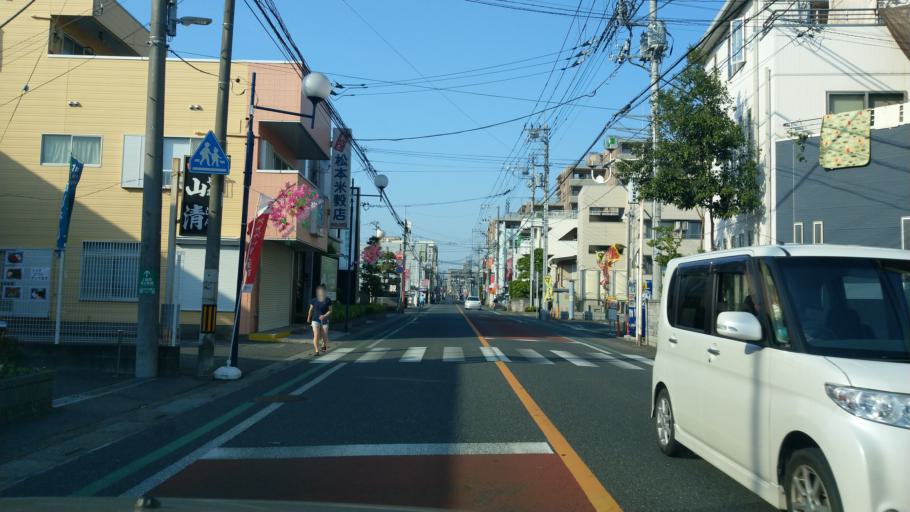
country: JP
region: Saitama
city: Kamifukuoka
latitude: 35.8673
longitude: 139.5101
